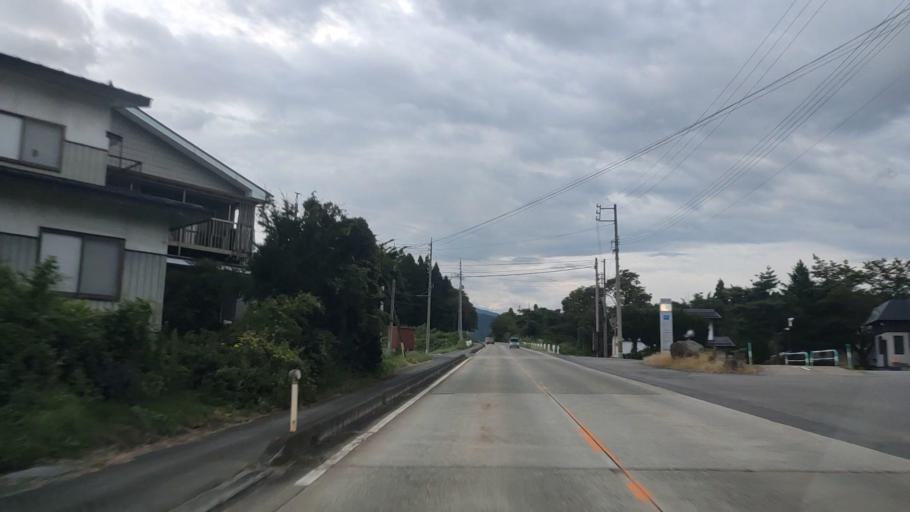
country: JP
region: Nagano
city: Iiyama
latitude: 36.8905
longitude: 138.4077
